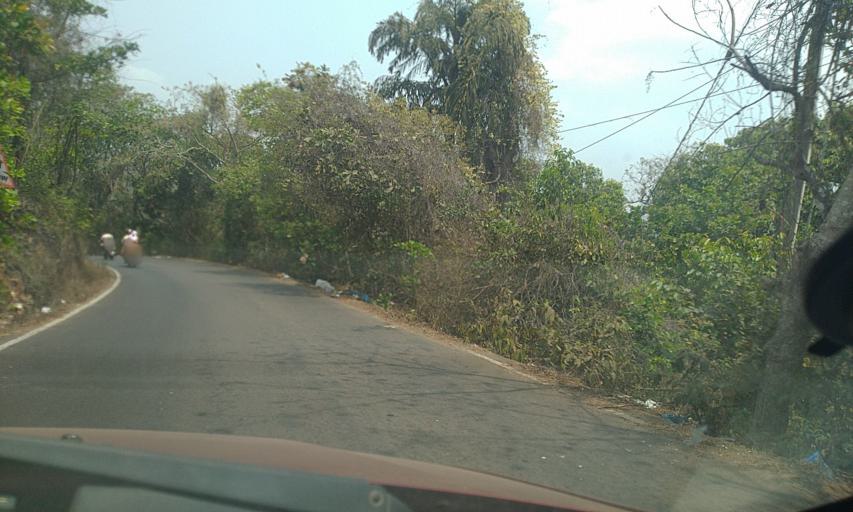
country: IN
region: Goa
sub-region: North Goa
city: Solim
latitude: 15.6143
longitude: 73.7922
